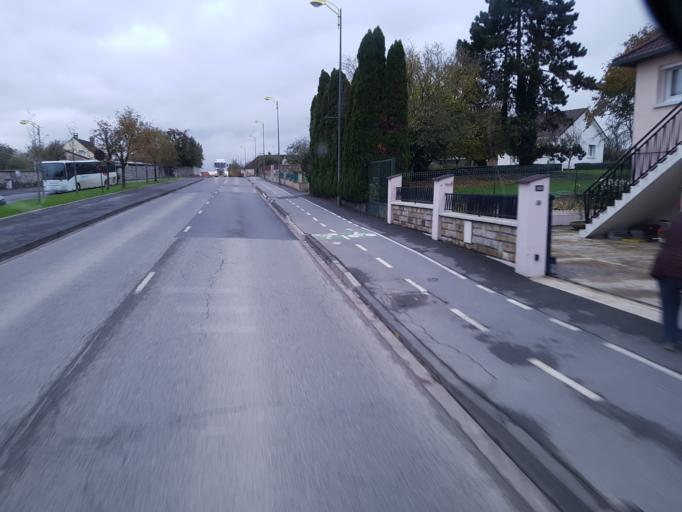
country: FR
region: Champagne-Ardenne
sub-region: Departement de la Marne
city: Montmirail
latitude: 48.8717
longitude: 3.5451
